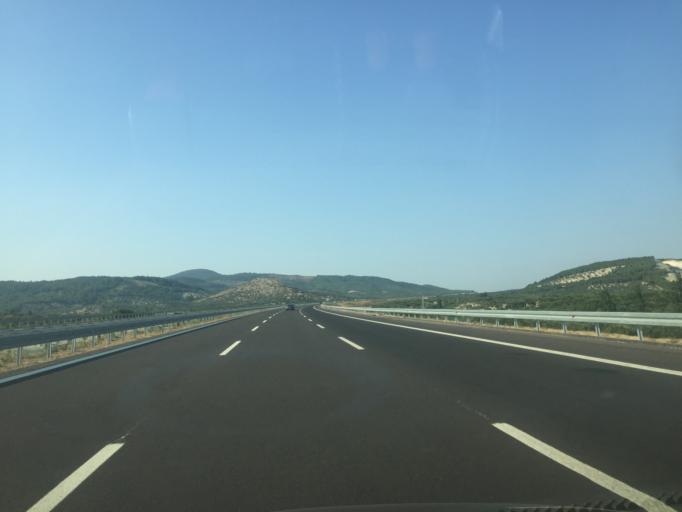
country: TR
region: Manisa
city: Zeytinliova
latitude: 38.9794
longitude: 27.7313
